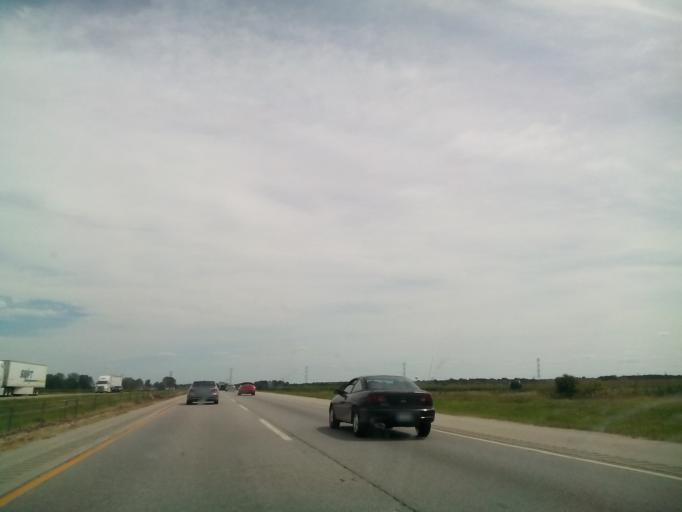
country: US
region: Illinois
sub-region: Kane County
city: Sugar Grove
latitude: 41.8131
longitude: -88.4500
